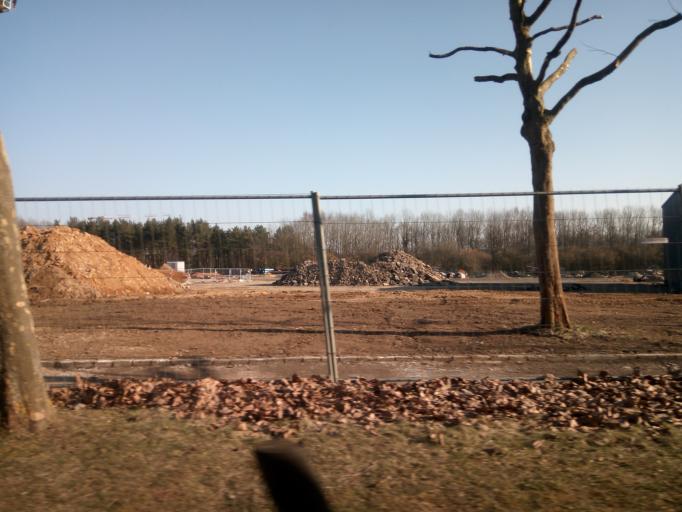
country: LU
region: Luxembourg
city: Kirchberg
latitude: 49.6307
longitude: 6.1591
